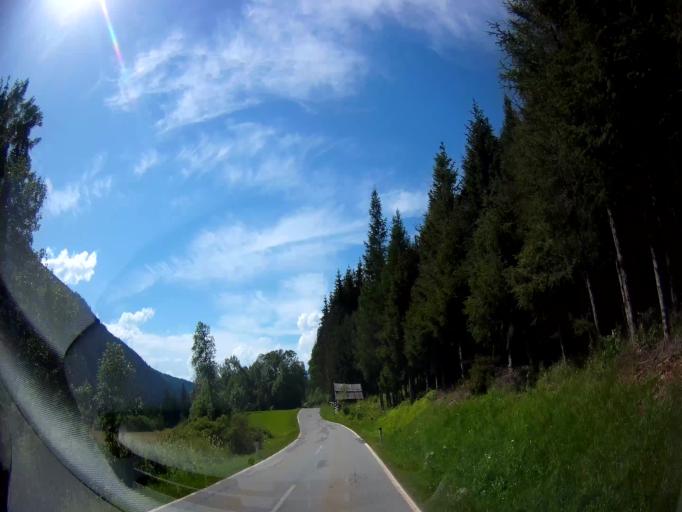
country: AT
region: Salzburg
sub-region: Politischer Bezirk Tamsweg
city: Thomatal
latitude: 47.0662
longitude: 13.7626
